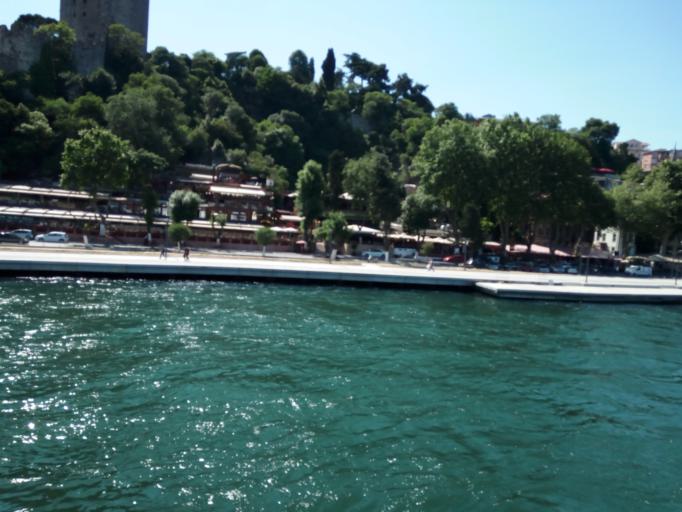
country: TR
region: Istanbul
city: UEskuedar
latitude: 41.0859
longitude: 29.0579
